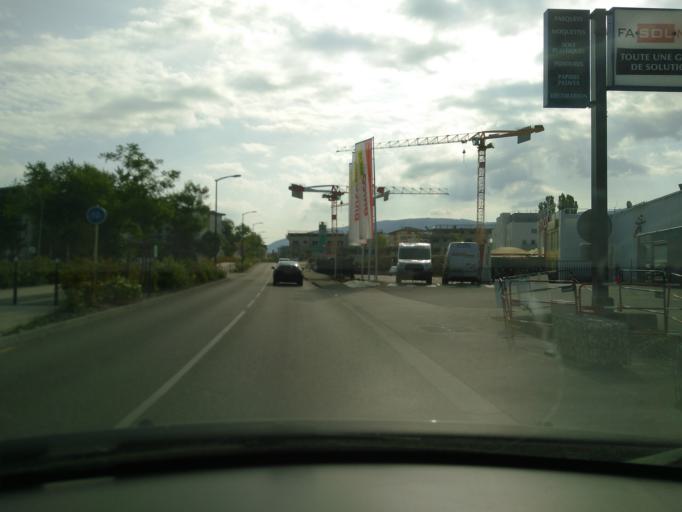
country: FR
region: Rhone-Alpes
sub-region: Departement de la Haute-Savoie
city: Saint-Julien-en-Genevois
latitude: 46.1394
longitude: 6.0719
